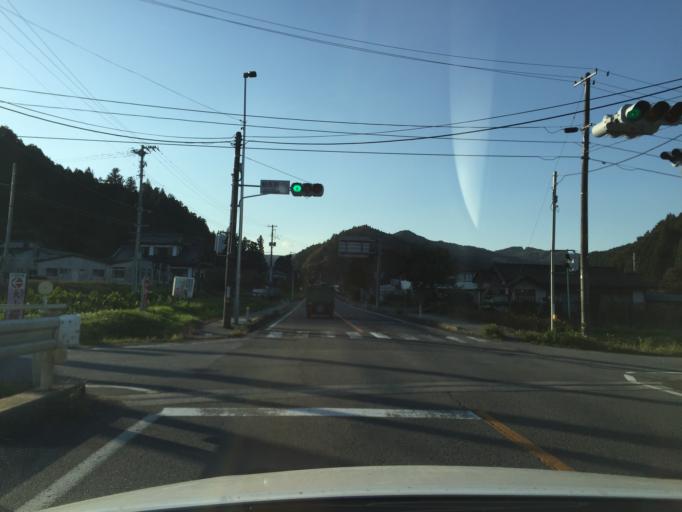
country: JP
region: Fukushima
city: Iwaki
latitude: 37.1425
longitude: 140.6852
